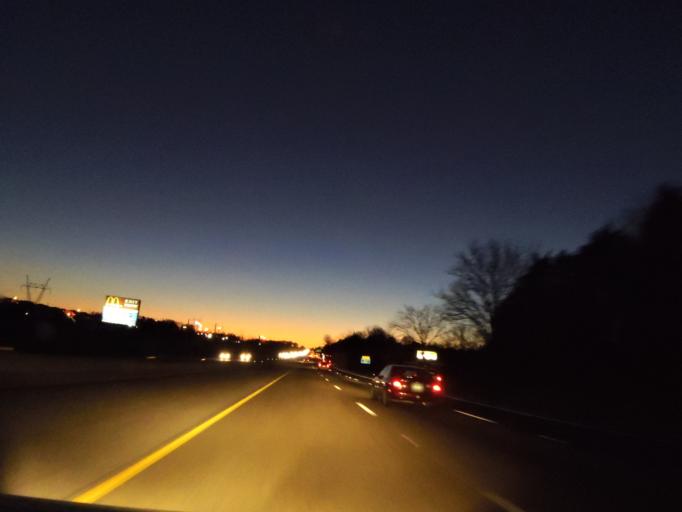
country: US
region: Tennessee
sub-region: Jefferson County
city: Dandridge
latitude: 36.0433
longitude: -83.4292
